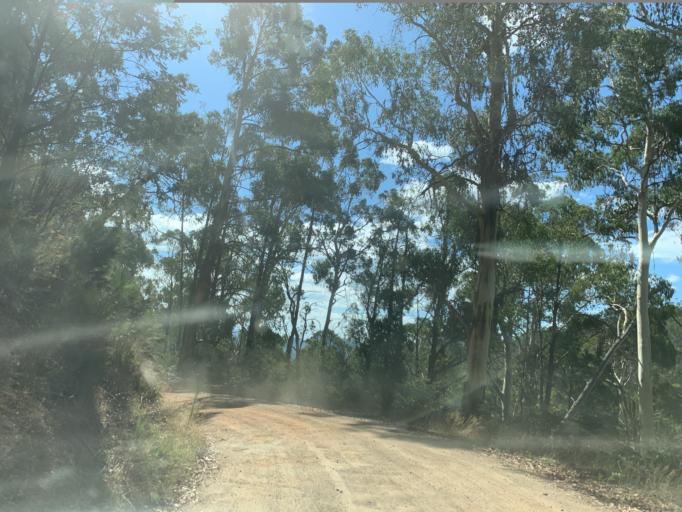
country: AU
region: Victoria
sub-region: Mansfield
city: Mansfield
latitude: -37.0945
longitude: 146.5247
